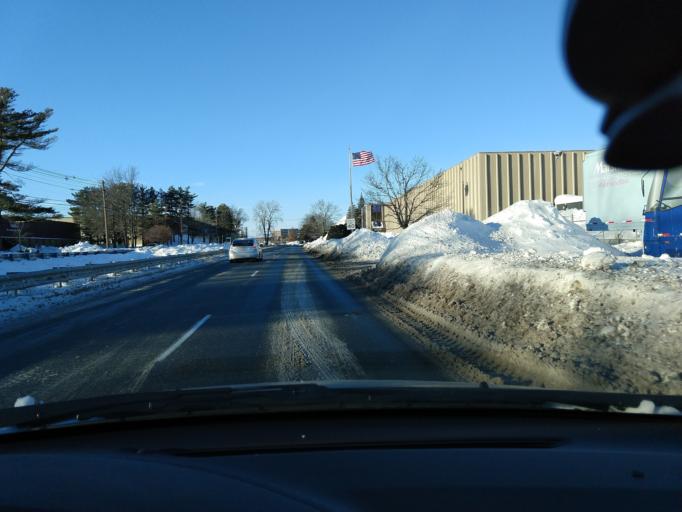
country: US
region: Massachusetts
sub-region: Middlesex County
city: Woburn
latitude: 42.5126
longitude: -71.1343
